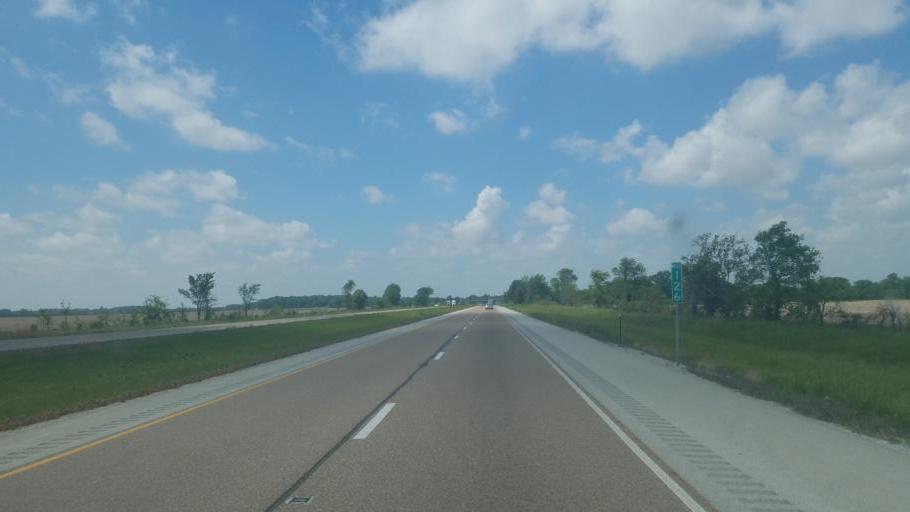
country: US
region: Illinois
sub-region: Clark County
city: Casey
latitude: 39.2929
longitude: -88.0373
